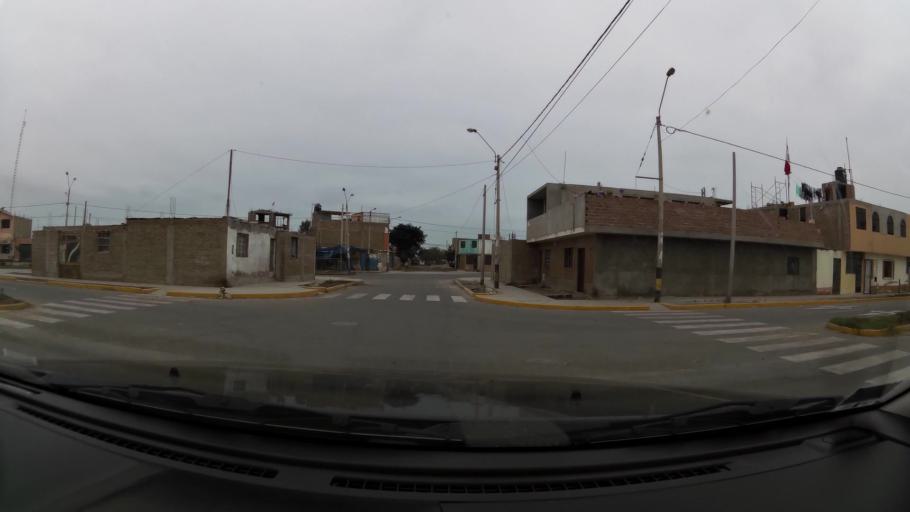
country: PE
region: Ica
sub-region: Provincia de Pisco
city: Pisco
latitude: -13.7212
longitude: -76.2053
